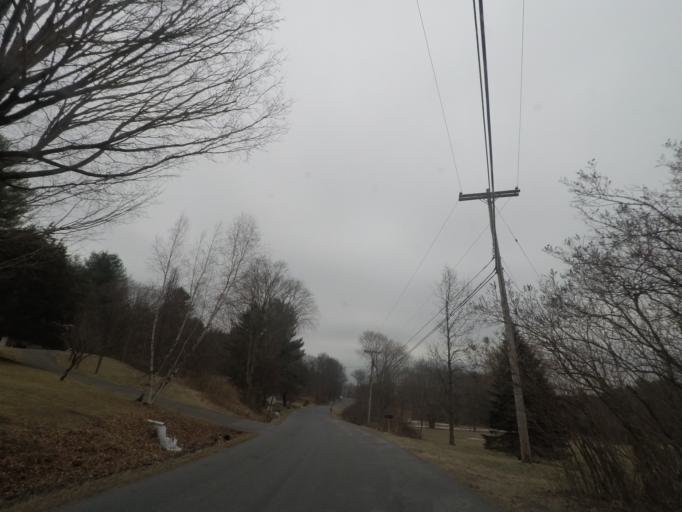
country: US
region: New York
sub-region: Rensselaer County
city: East Greenbush
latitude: 42.5651
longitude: -73.6592
